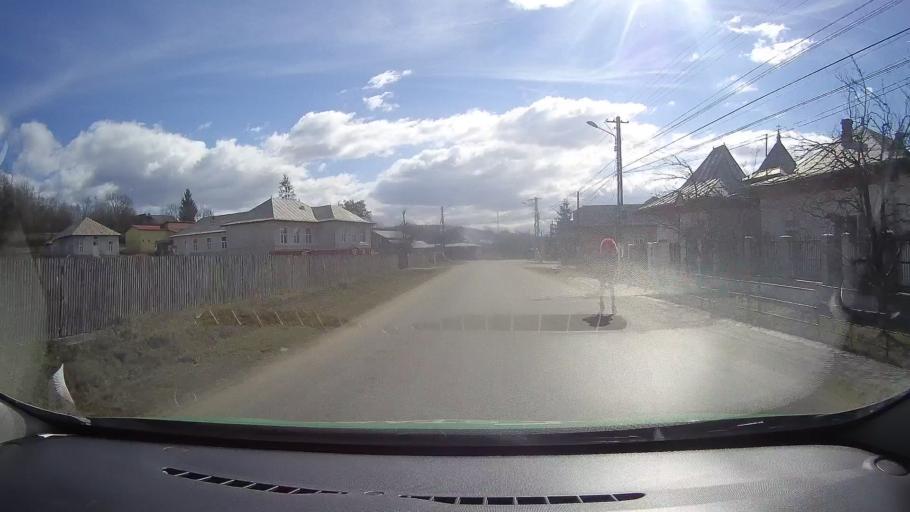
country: RO
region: Dambovita
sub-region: Comuna Vulcana-Pandele
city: Gura Vulcanei
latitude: 45.0306
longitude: 25.3947
